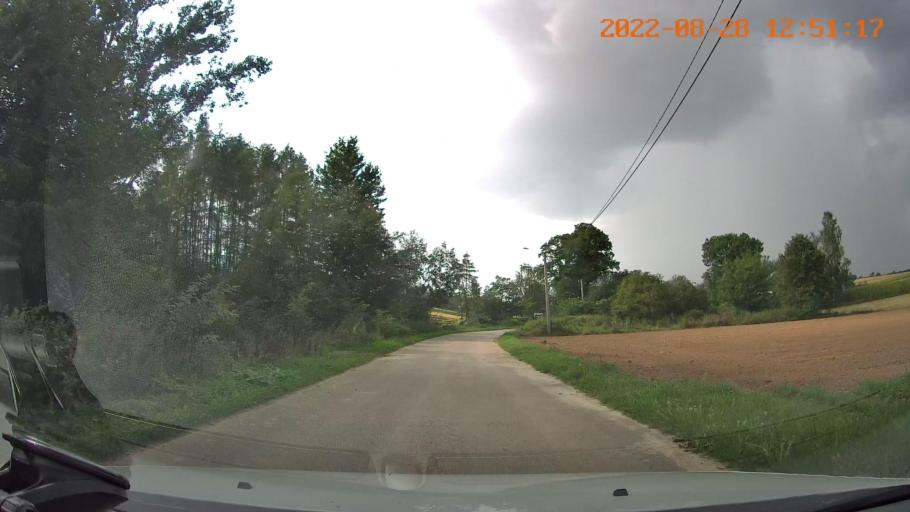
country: PL
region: Swietokrzyskie
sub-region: Powiat pinczowski
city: Dzialoszyce
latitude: 50.3641
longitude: 20.2477
